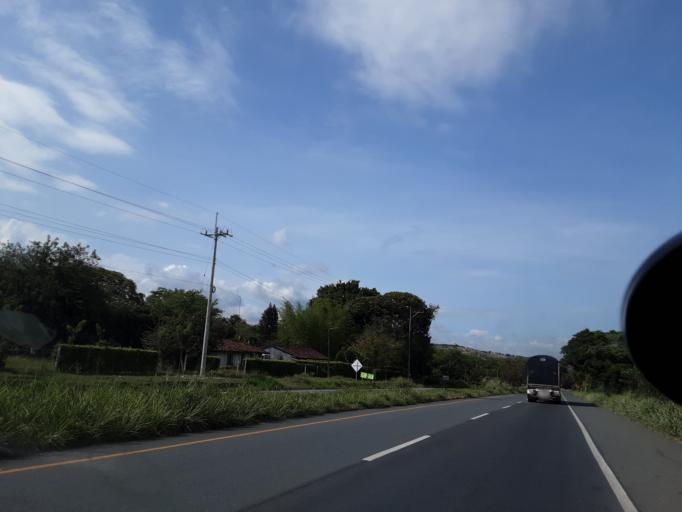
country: CO
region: Valle del Cauca
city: Buga
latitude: 3.8433
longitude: -76.2993
